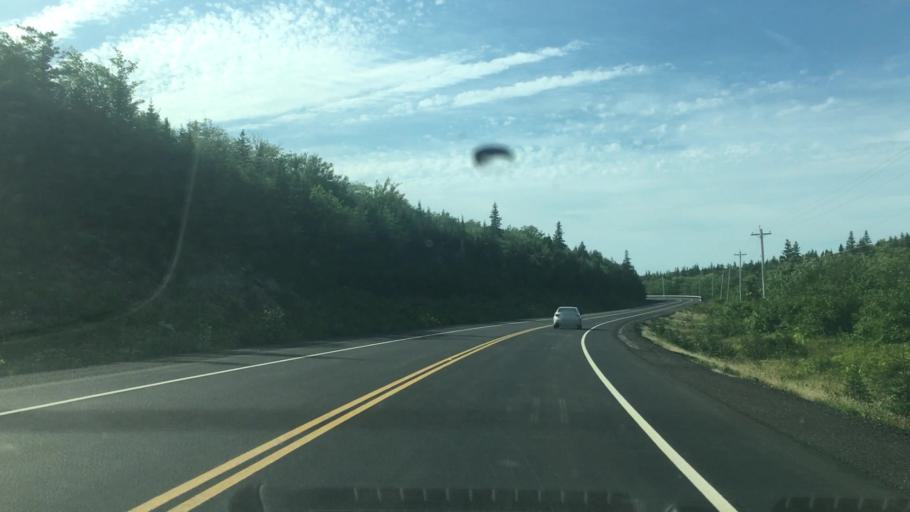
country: CA
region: Nova Scotia
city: Sydney Mines
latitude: 46.8378
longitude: -60.3849
